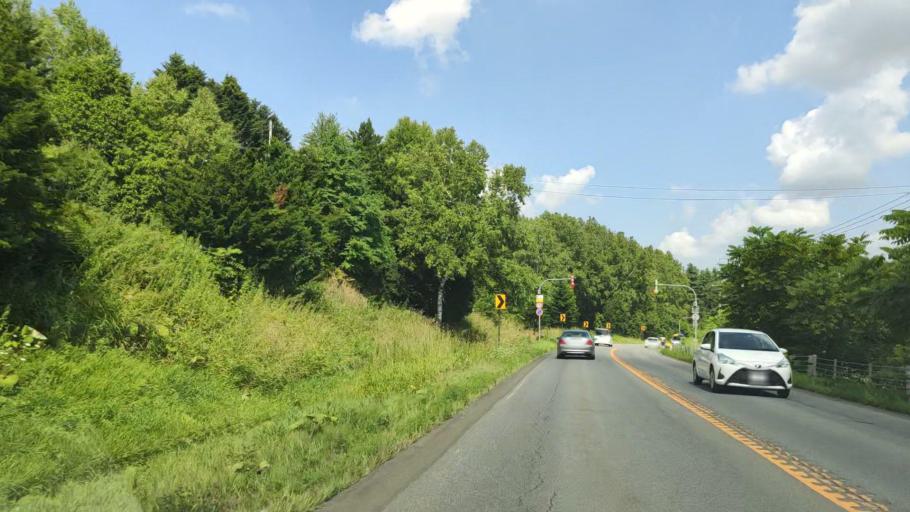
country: JP
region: Hokkaido
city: Shimo-furano
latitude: 43.5558
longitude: 142.4354
